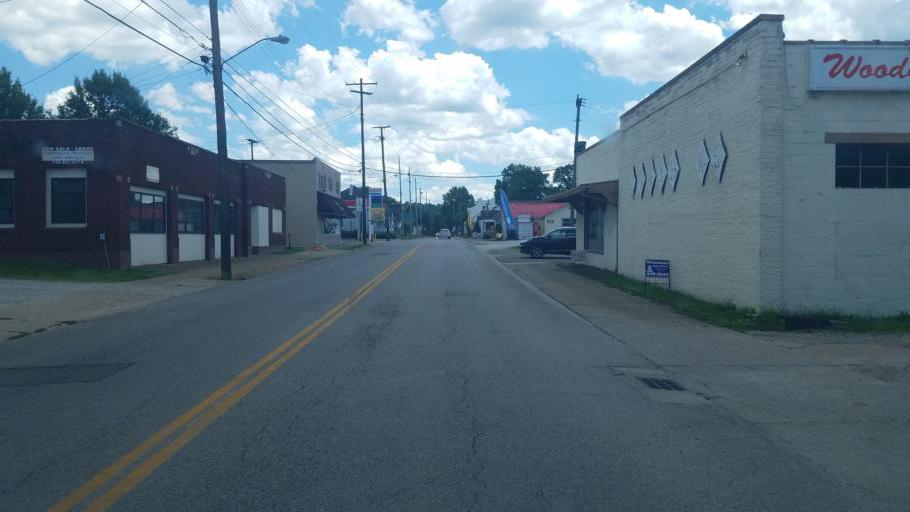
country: US
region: Ohio
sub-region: Gallia County
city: Gallipolis
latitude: 38.8054
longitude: -82.2131
